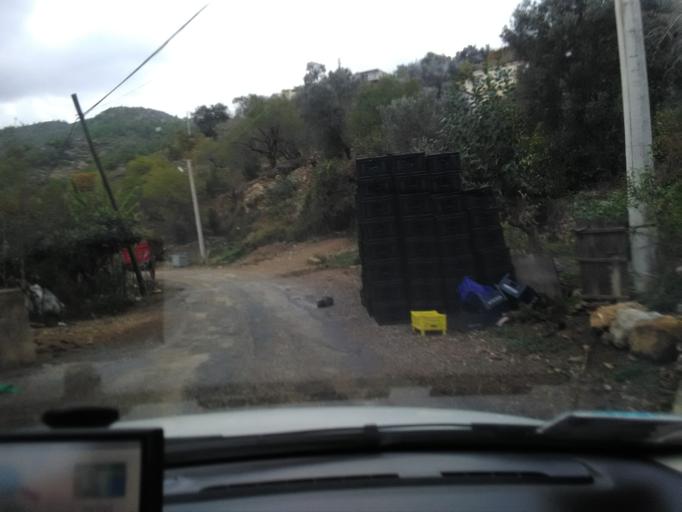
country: TR
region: Antalya
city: Gazipasa
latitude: 36.1559
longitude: 32.4253
